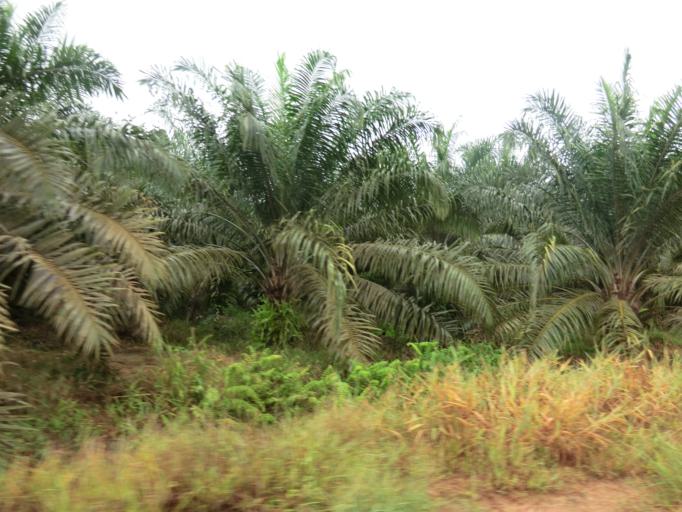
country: MY
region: Sarawak
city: Simanggang
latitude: 0.9913
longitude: 111.8863
